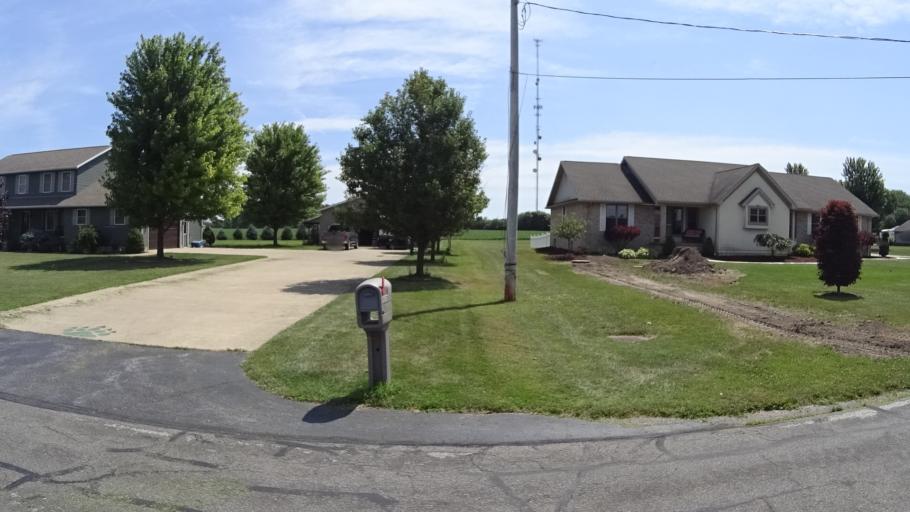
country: US
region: Ohio
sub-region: Erie County
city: Sandusky
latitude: 41.4062
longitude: -82.7884
